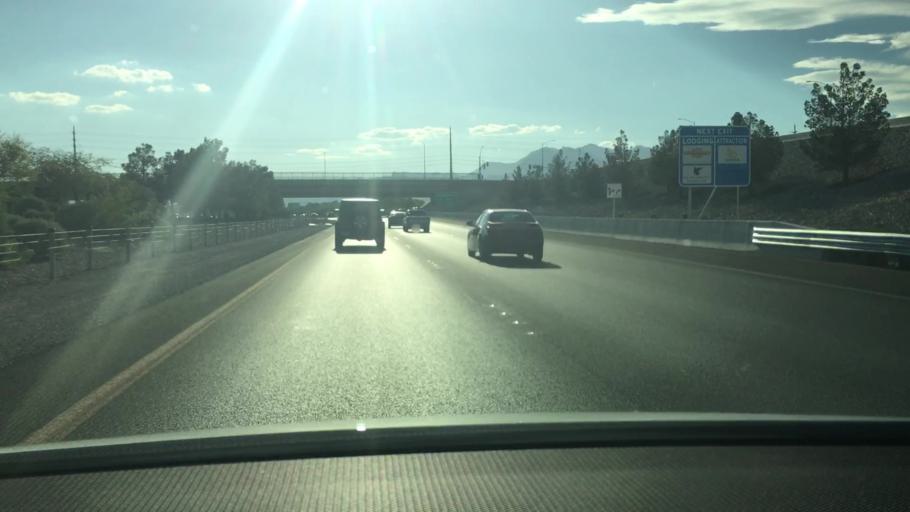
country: US
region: Nevada
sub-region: Clark County
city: Spring Valley
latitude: 36.1782
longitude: -115.2758
